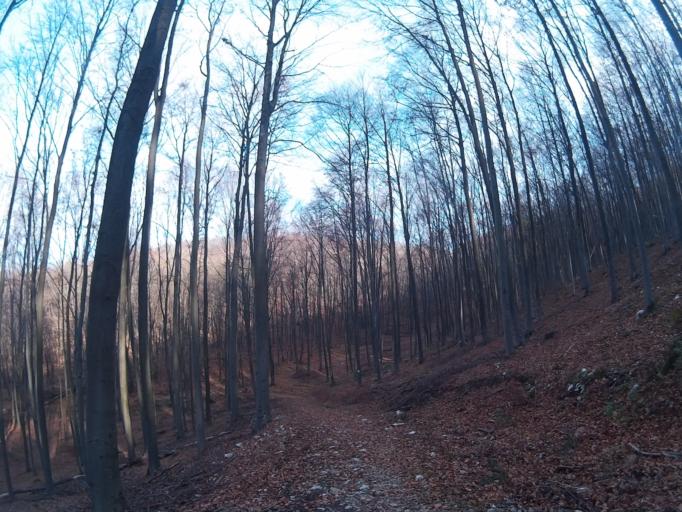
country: HU
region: Heves
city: Belapatfalva
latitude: 48.0536
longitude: 20.4033
